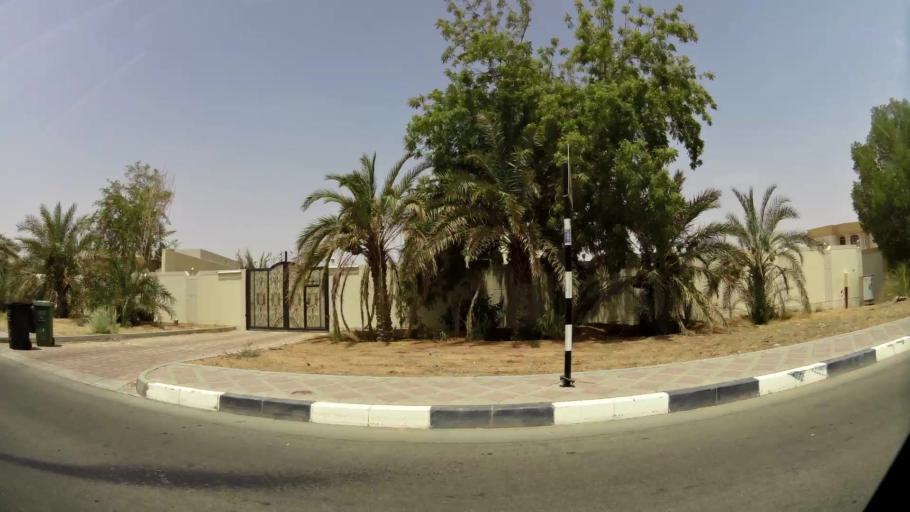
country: AE
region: Abu Dhabi
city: Al Ain
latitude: 24.1951
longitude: 55.7371
